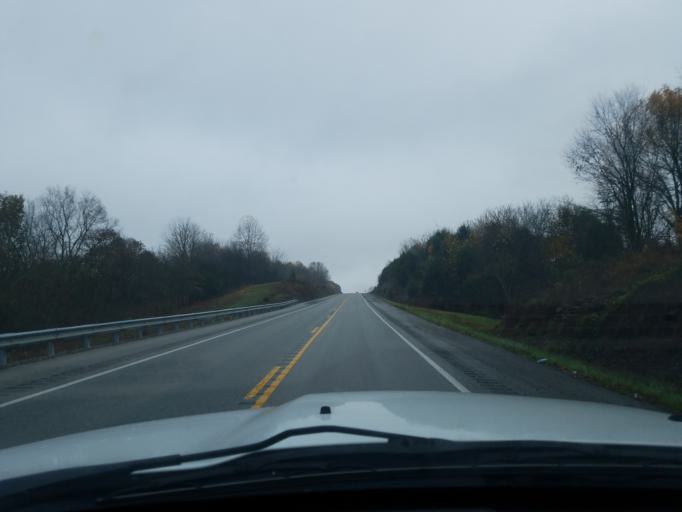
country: US
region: Kentucky
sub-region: Taylor County
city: Campbellsville
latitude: 37.3899
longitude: -85.4267
